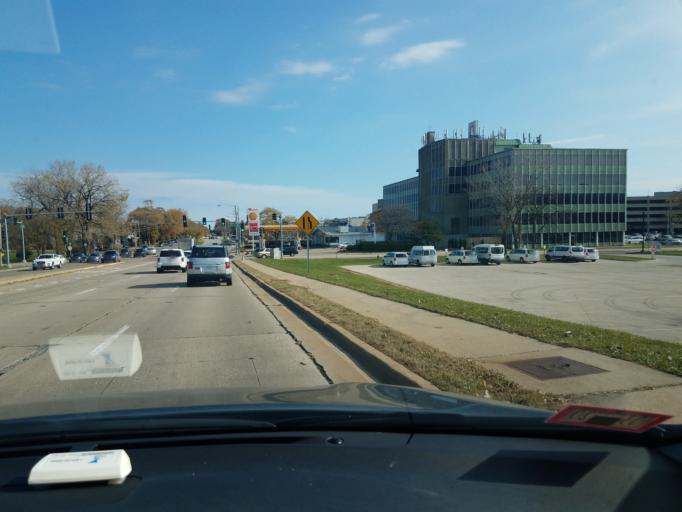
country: US
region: Illinois
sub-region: Cook County
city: Wilmette
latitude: 42.0624
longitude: -87.7538
